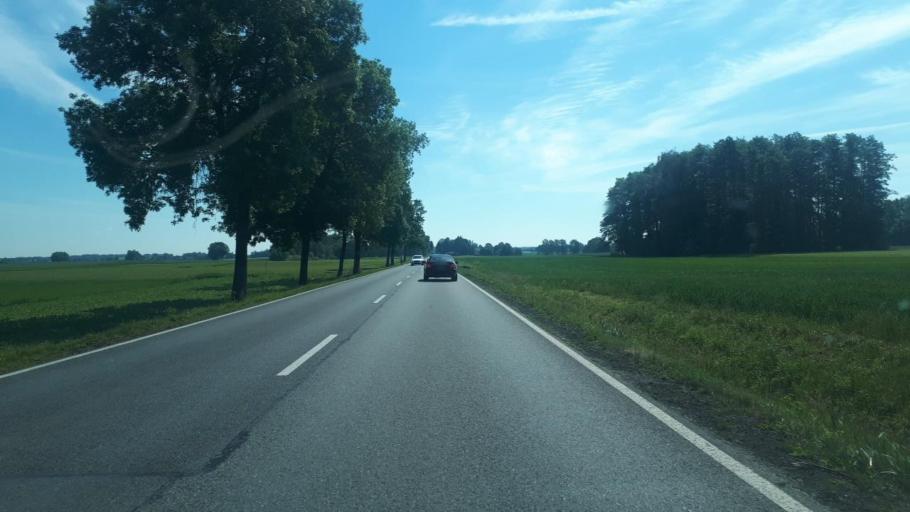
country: PL
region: Silesian Voivodeship
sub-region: Powiat pszczynski
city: Miedzna
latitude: 49.9698
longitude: 19.0628
